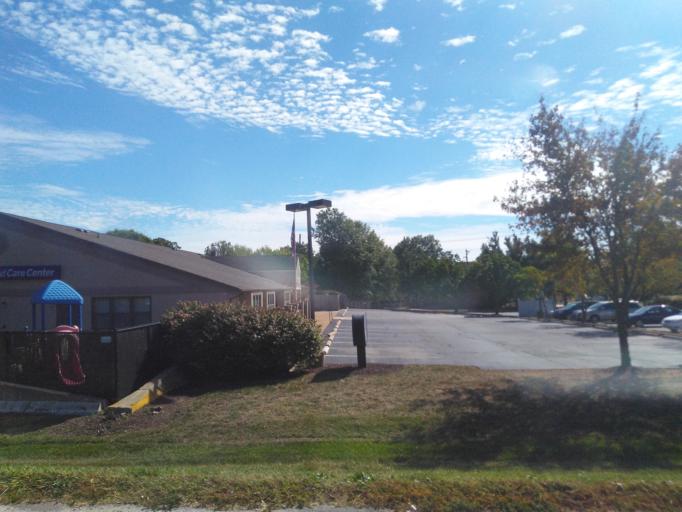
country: US
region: Missouri
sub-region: Saint Louis County
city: Concord
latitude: 38.5028
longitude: -90.3803
